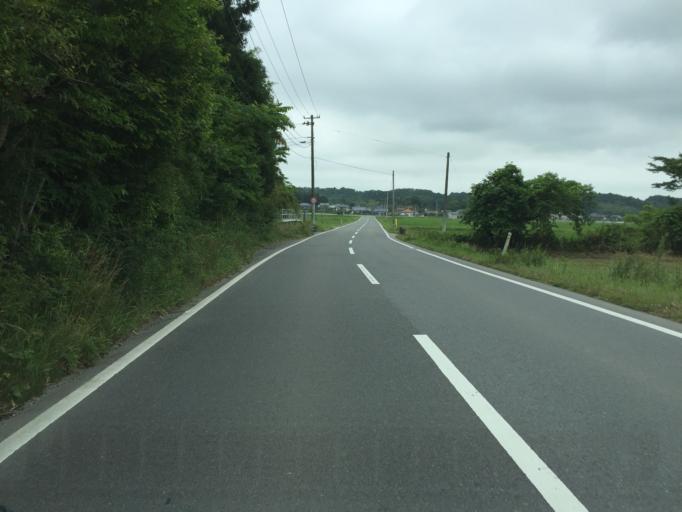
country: JP
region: Miyagi
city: Marumori
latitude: 37.7473
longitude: 140.9157
